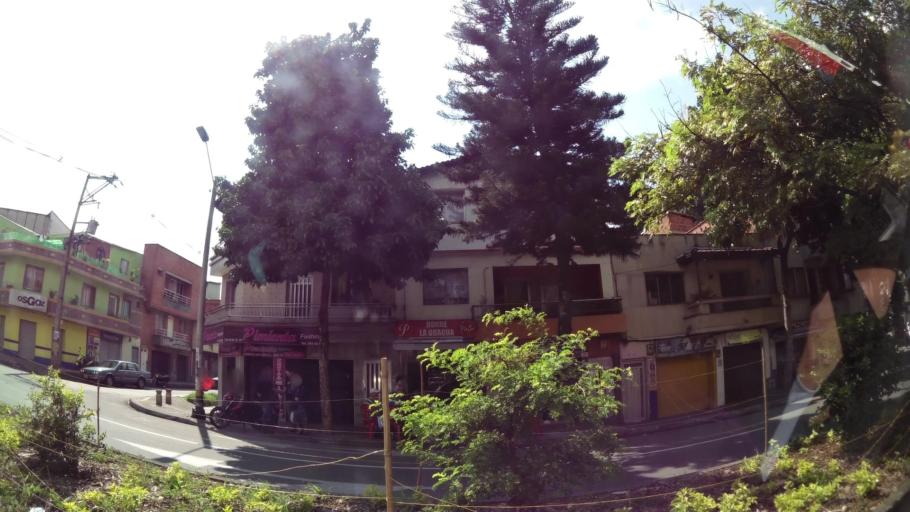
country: CO
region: Antioquia
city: Medellin
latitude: 6.2289
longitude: -75.5963
